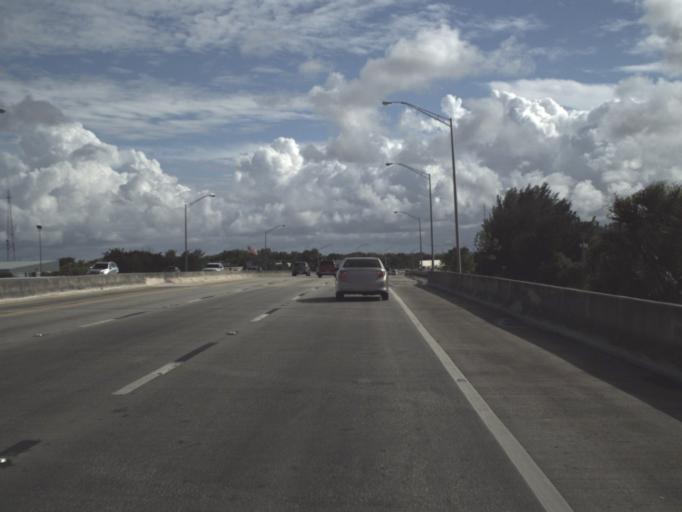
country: US
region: Florida
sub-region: Broward County
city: Coconut Creek
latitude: 26.2601
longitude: -80.1675
